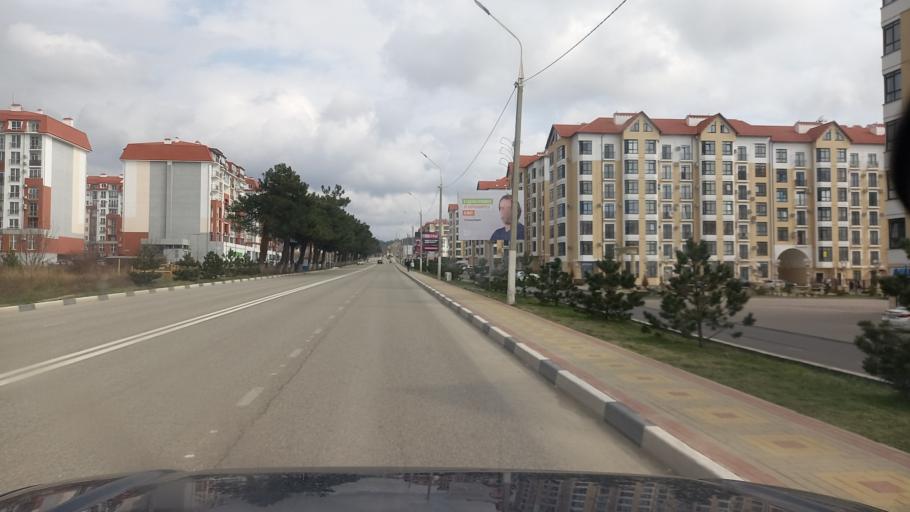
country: RU
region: Krasnodarskiy
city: Gelendzhik
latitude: 44.5573
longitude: 38.1030
